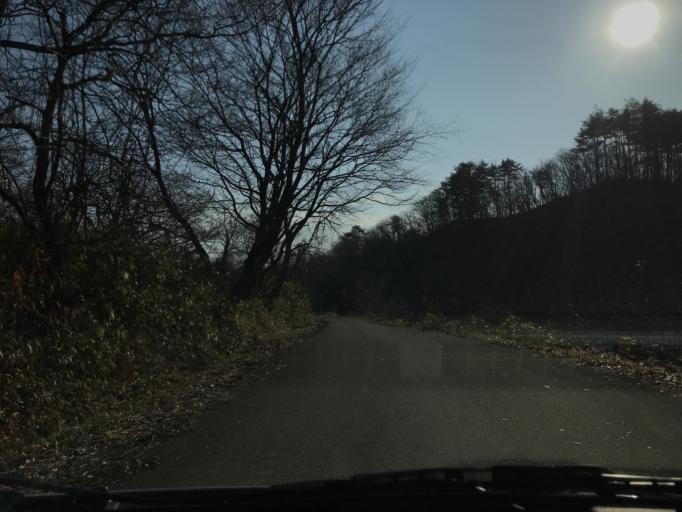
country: JP
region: Iwate
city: Ichinoseki
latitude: 38.9724
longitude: 141.0544
